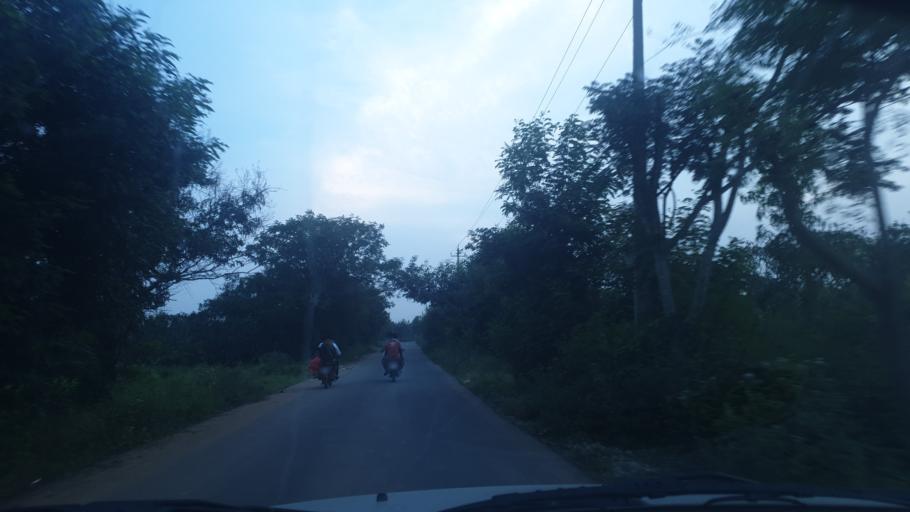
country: IN
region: Karnataka
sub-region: Bangalore Rural
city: Hoskote
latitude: 13.0823
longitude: 77.7027
